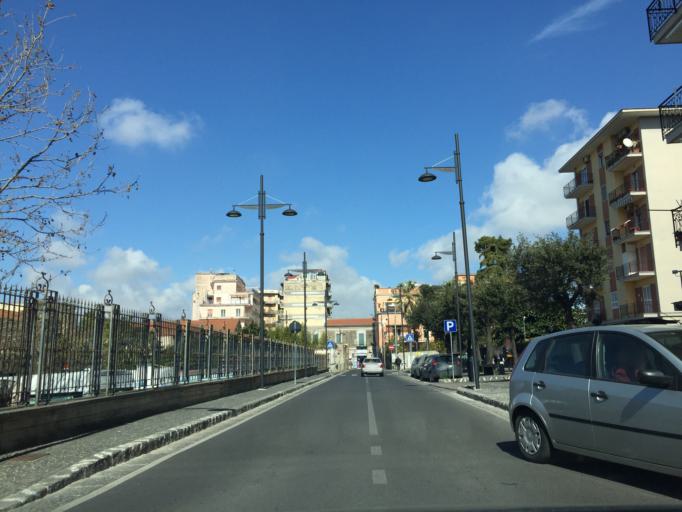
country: IT
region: Campania
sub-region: Provincia di Napoli
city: San Giorgio a Cremano
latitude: 40.8269
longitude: 14.3404
